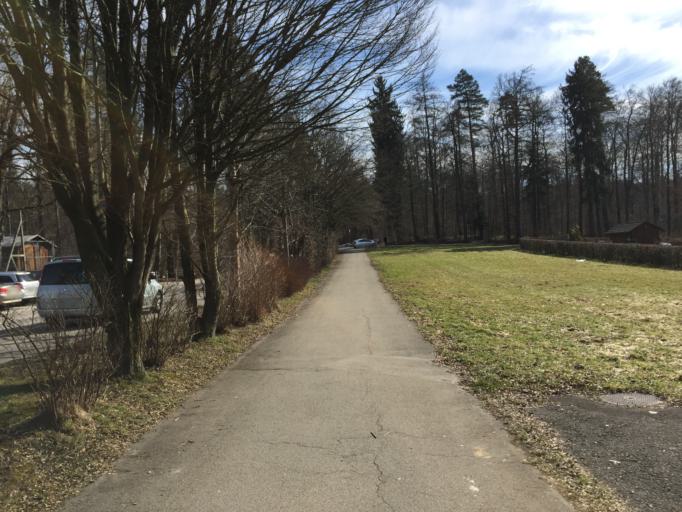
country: CH
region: Zurich
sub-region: Bezirk Zuerich
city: Zuerich (Kreis 7)
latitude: 47.3800
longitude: 8.5731
